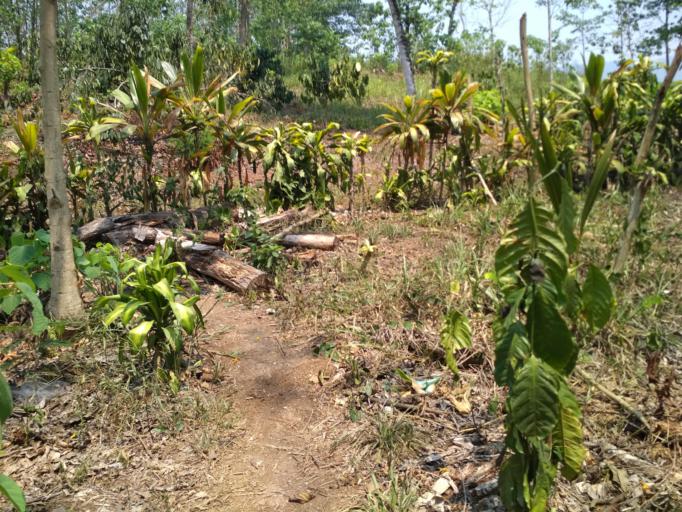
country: MX
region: Veracruz
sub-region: Tezonapa
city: Laguna Chica (Pueblo Nuevo)
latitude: 18.5569
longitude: -96.7279
